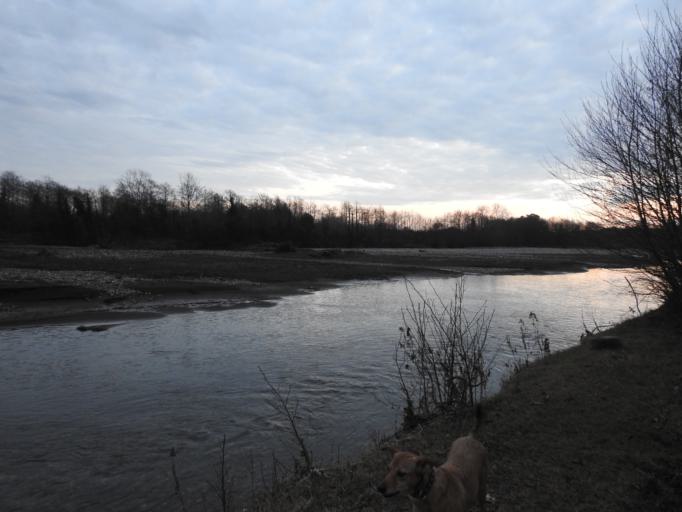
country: GE
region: Abkhazia
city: Och'amch'ire
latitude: 42.7021
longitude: 41.4751
